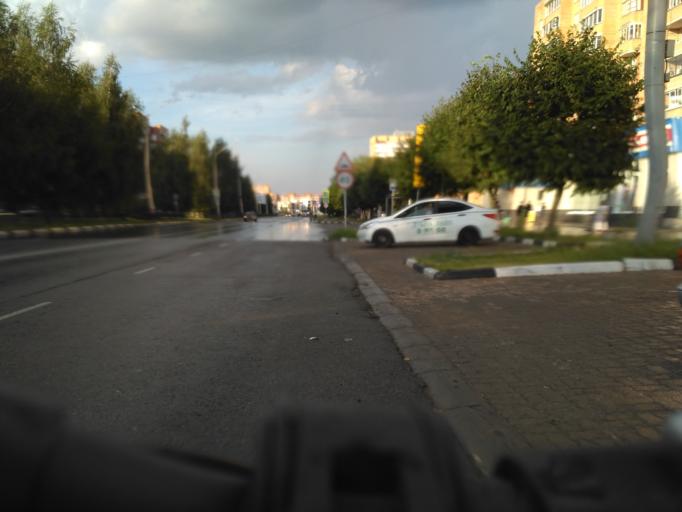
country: RU
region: Moskovskaya
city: Dubna
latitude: 56.7322
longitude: 37.1502
